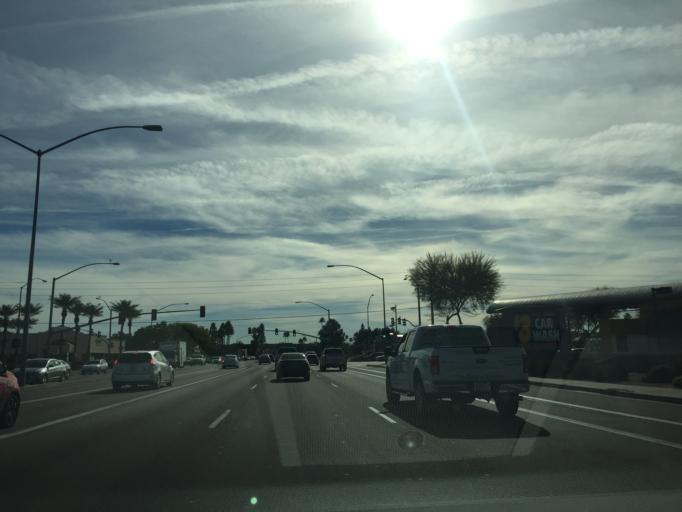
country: US
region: Arizona
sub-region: Maricopa County
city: Gilbert
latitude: 33.3798
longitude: -111.7885
